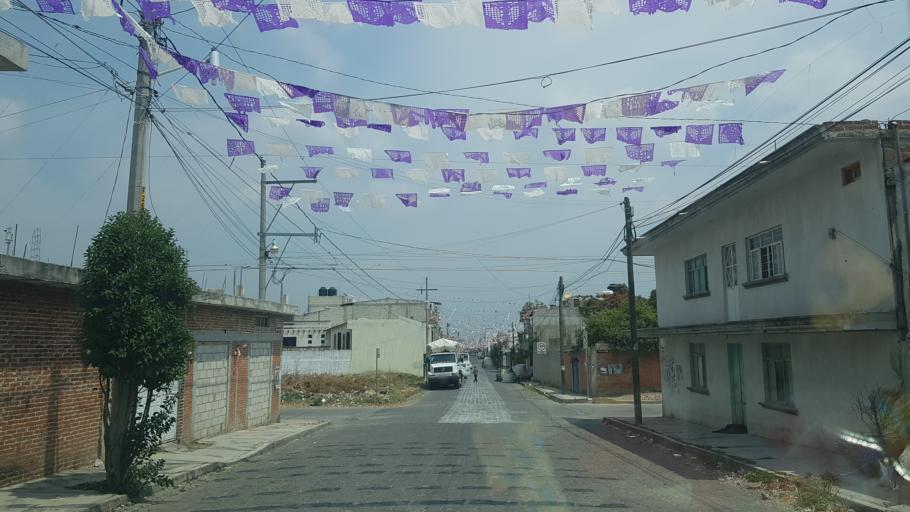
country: MX
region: Puebla
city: Huejotzingo
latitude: 19.1512
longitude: -98.4099
